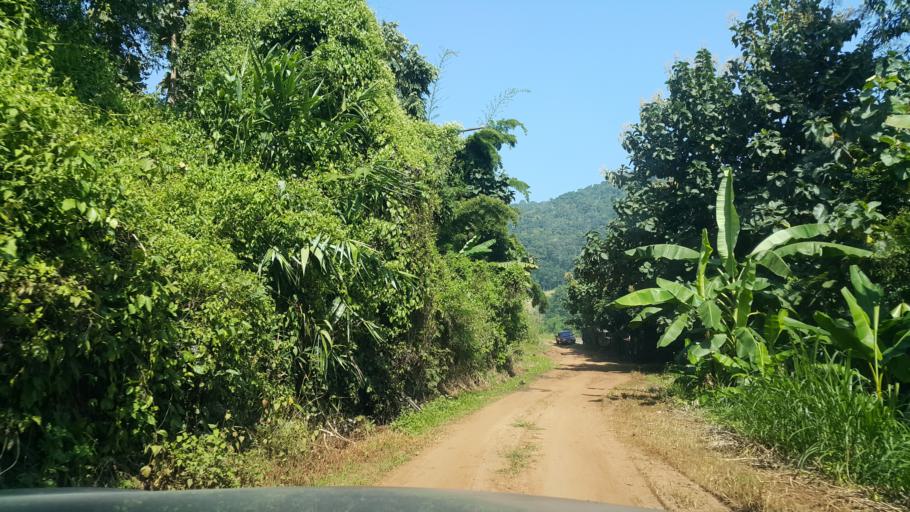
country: TH
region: Chiang Mai
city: Samoeng
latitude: 18.9423
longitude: 98.6196
